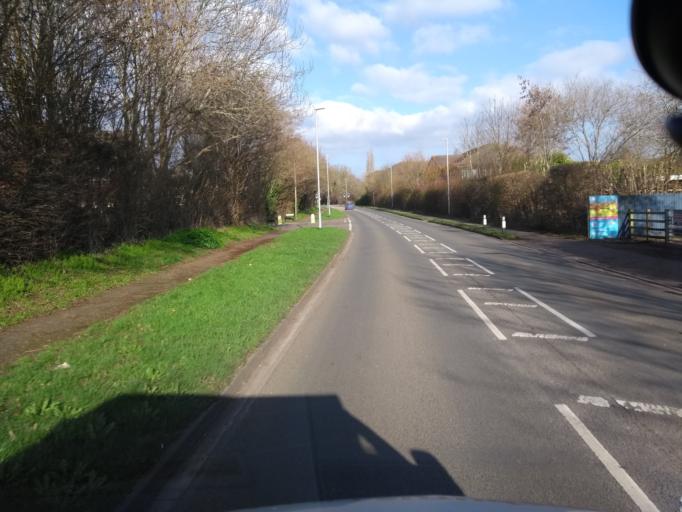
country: GB
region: England
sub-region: Somerset
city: Taunton
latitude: 51.0133
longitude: -3.0699
